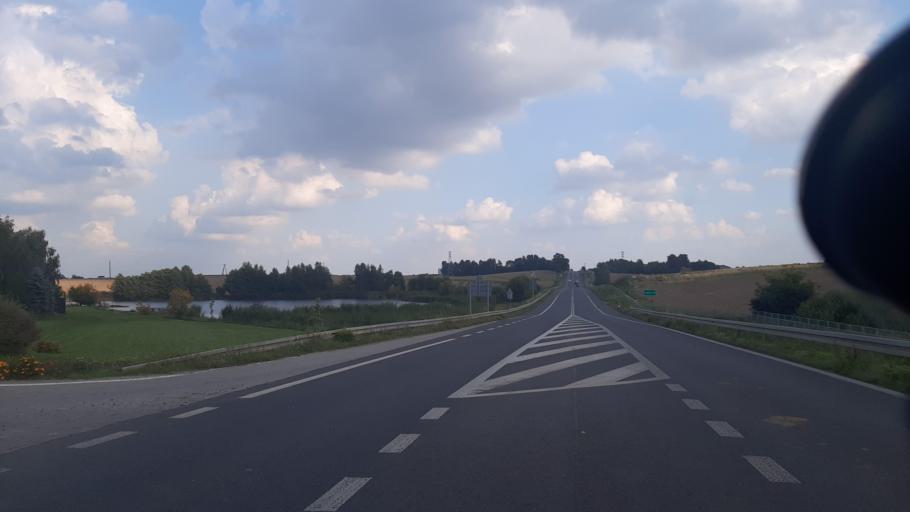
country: PL
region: Lublin Voivodeship
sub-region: Powiat lubelski
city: Garbow
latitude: 51.3430
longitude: 22.3650
